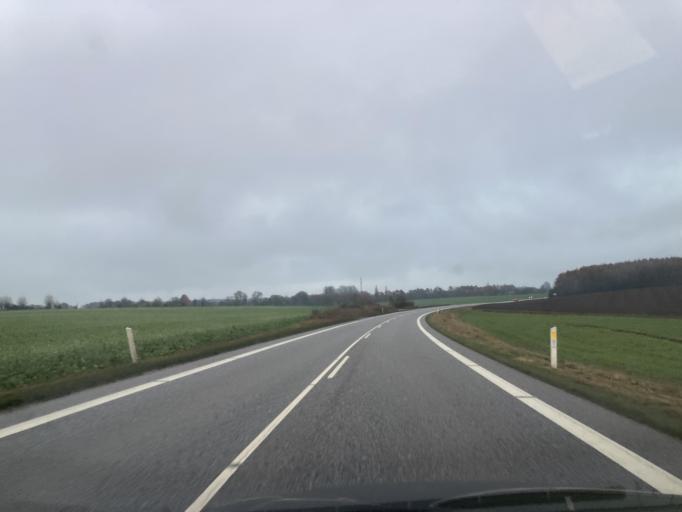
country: DK
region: Zealand
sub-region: Lolland Kommune
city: Holeby
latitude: 54.7148
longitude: 11.4412
